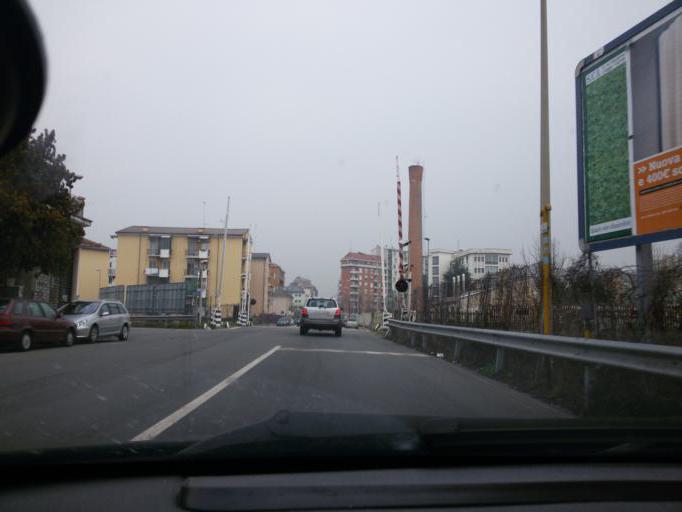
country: IT
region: Piedmont
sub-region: Provincia di Vercelli
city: Vercelli
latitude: 45.3168
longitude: 8.4106
